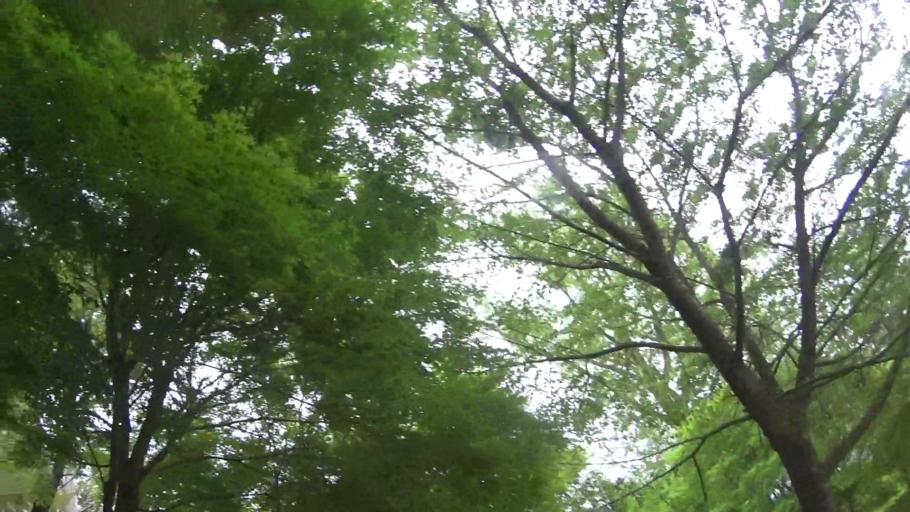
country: JP
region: Kyoto
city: Maizuru
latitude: 35.3889
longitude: 135.4420
